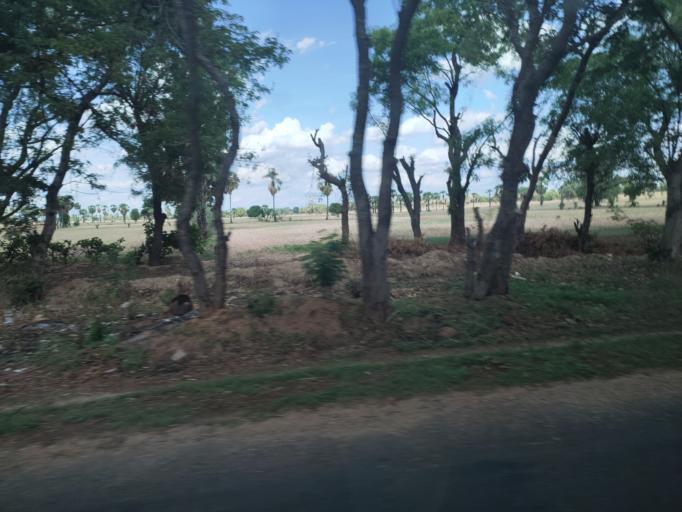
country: MM
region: Magway
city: Magway
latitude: 20.2155
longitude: 95.0173
